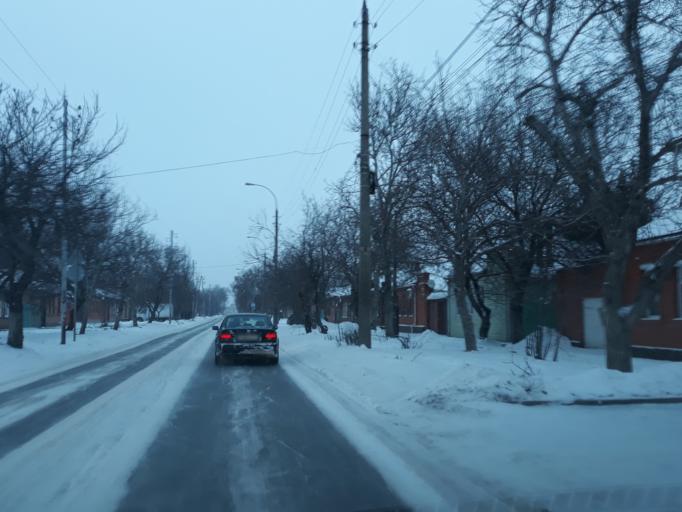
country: RU
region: Rostov
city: Taganrog
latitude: 47.2556
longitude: 38.9384
